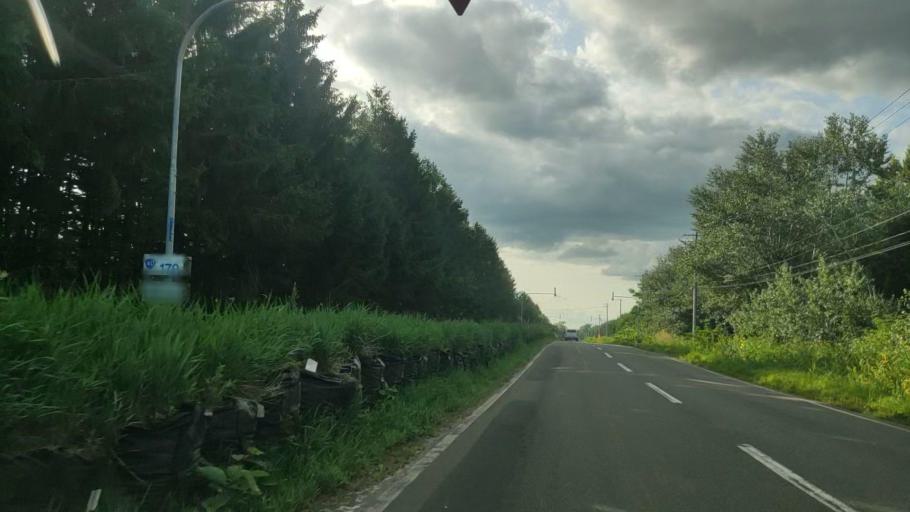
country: JP
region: Hokkaido
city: Makubetsu
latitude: 44.9005
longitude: 141.9117
